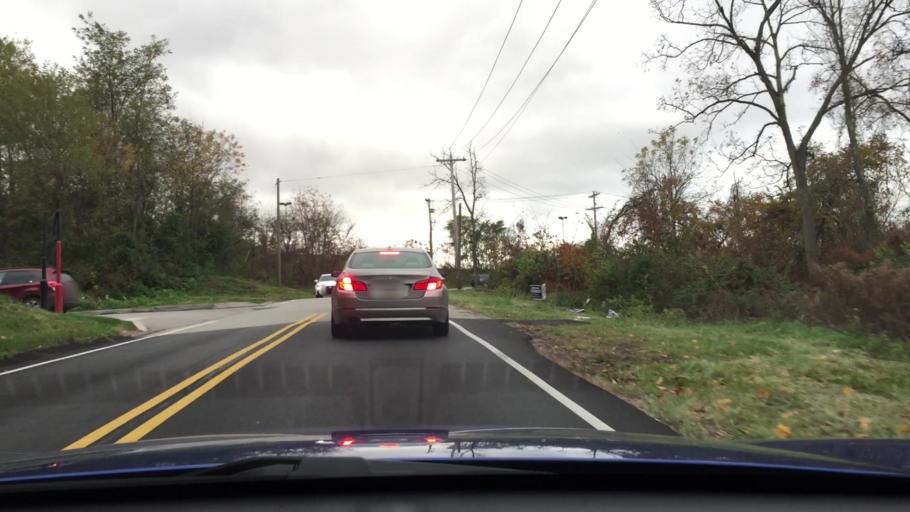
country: US
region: Pennsylvania
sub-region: Washington County
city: East Washington
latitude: 40.1923
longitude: -80.2272
